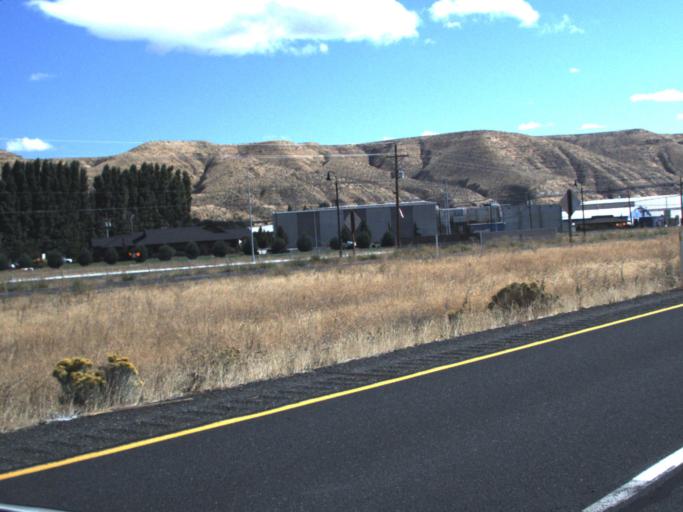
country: US
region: Washington
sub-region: Yakima County
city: Tieton
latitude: 46.7197
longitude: -120.6821
